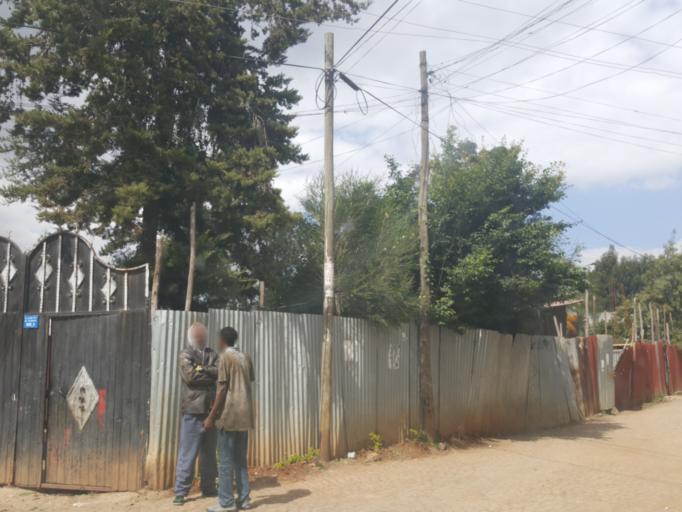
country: ET
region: Adis Abeba
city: Addis Ababa
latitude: 9.0616
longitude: 38.7177
